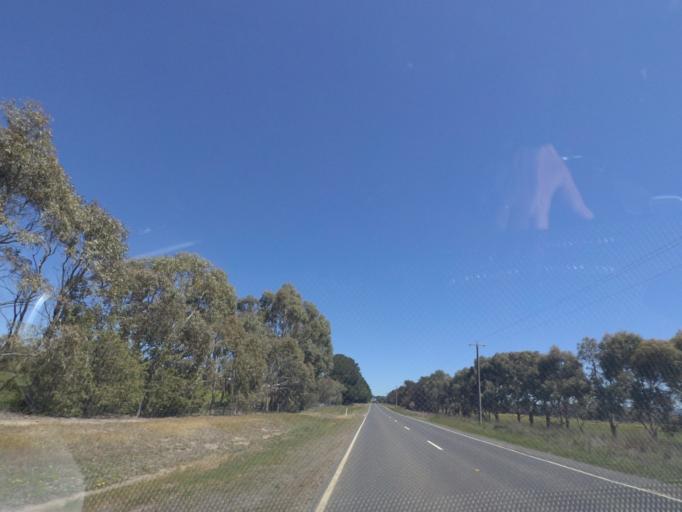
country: AU
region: Victoria
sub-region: Hume
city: Sunbury
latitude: -37.2850
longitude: 144.7663
